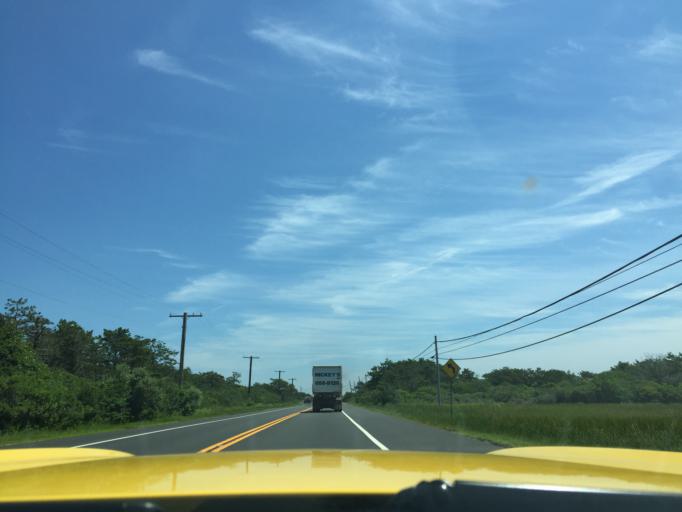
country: US
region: New York
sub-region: Suffolk County
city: Montauk
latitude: 41.0032
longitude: -72.0287
